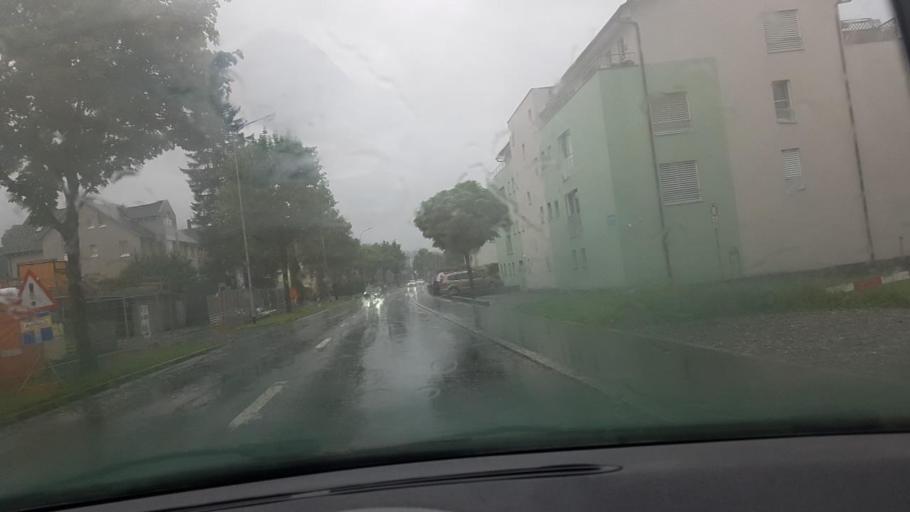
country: LI
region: Triesen
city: Triesen
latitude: 47.1019
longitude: 9.5248
